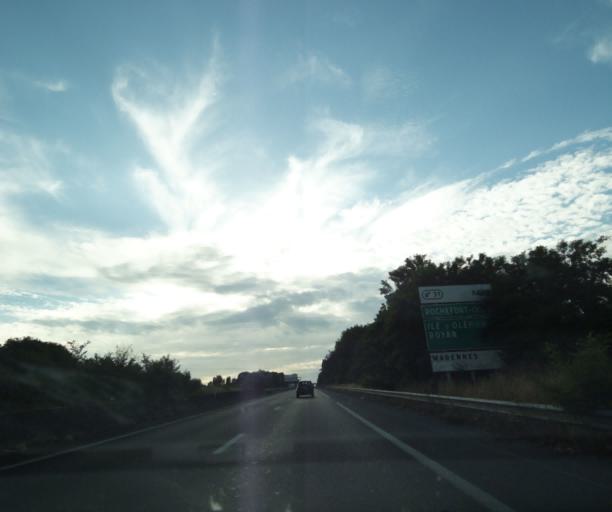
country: FR
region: Poitou-Charentes
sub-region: Departement de la Charente-Maritime
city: Breuil-Magne
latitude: 45.9633
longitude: -0.9636
